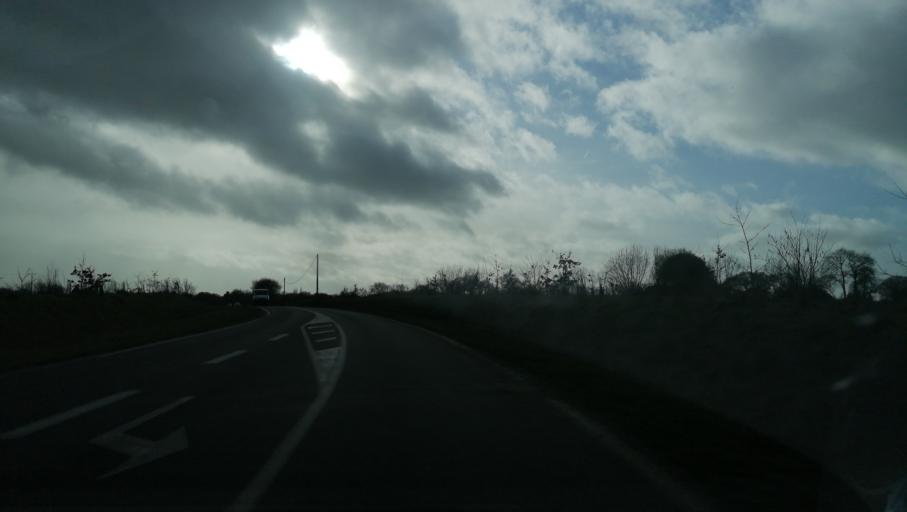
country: FR
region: Brittany
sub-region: Departement des Cotes-d'Armor
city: Lantic
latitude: 48.5883
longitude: -2.9146
